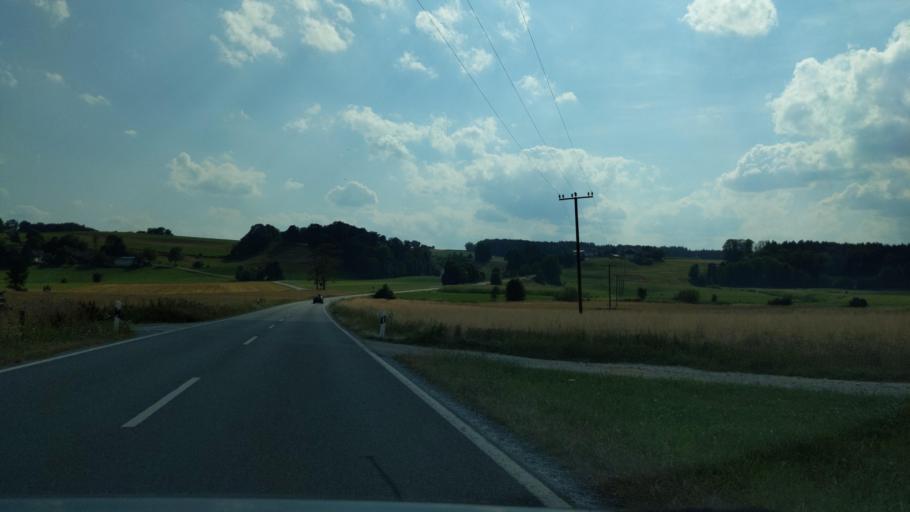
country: DE
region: Bavaria
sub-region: Upper Bavaria
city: Bruck
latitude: 48.0215
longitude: 11.9061
